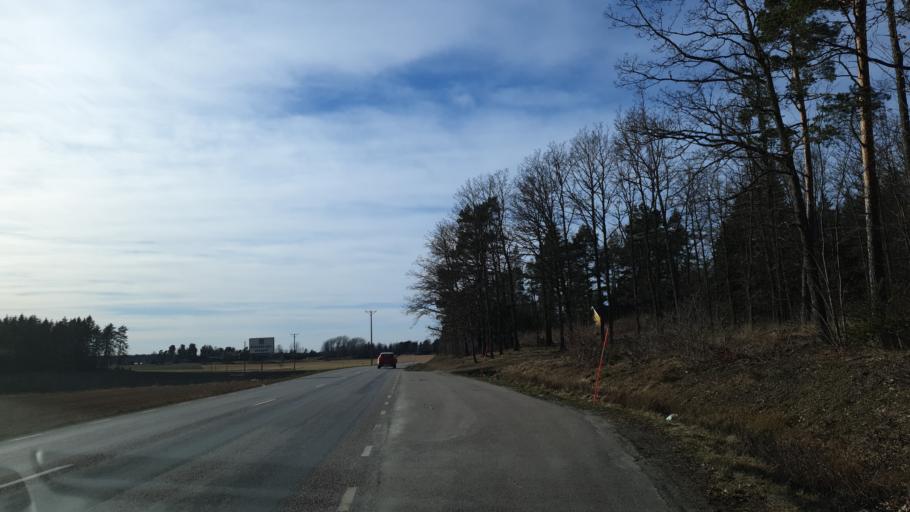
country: SE
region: Uppsala
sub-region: Enkopings Kommun
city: Grillby
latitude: 59.5972
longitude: 17.1630
